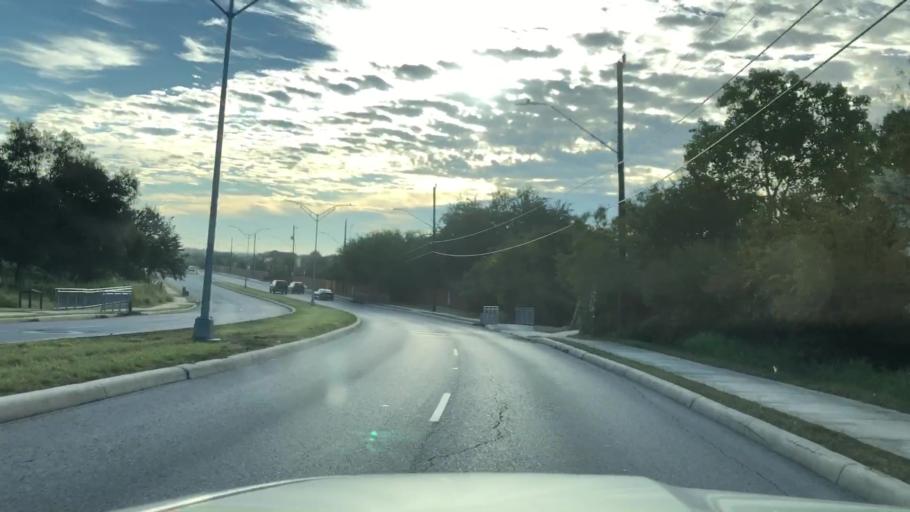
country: US
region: Texas
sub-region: Bexar County
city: Leon Valley
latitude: 29.5416
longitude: -98.6360
